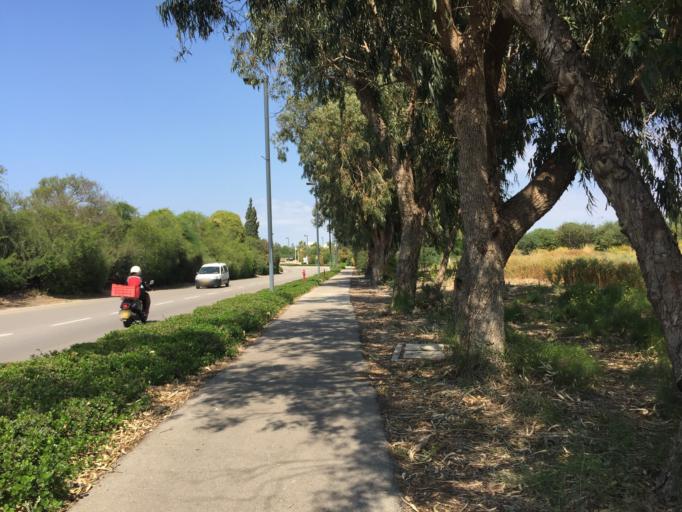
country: IL
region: Haifa
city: Qesarya
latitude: 32.5008
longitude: 34.9042
